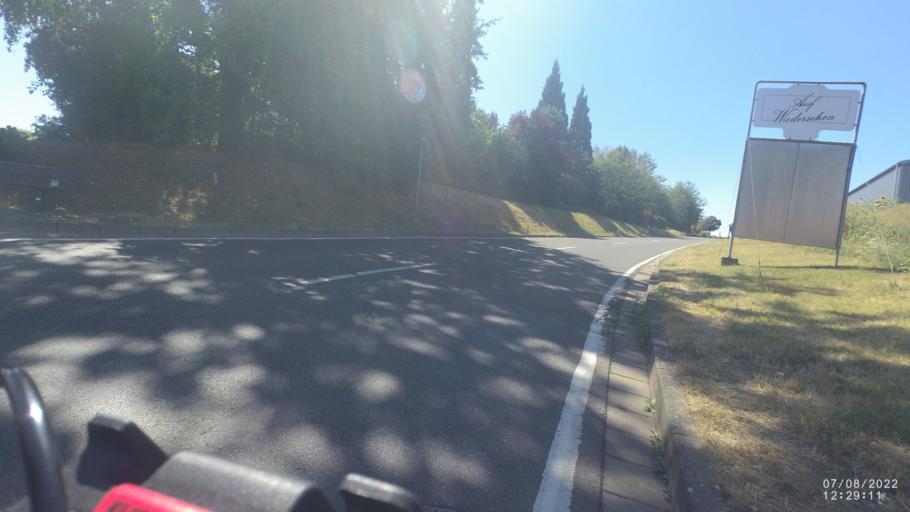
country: DE
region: Rheinland-Pfalz
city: Udenheim
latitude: 49.8629
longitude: 8.1726
